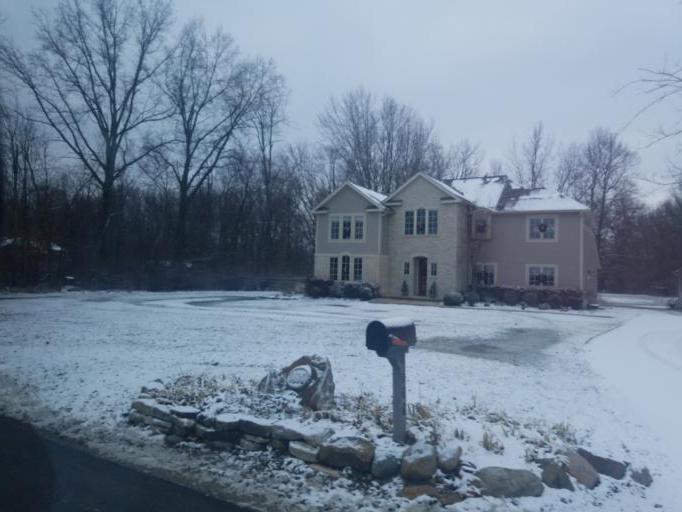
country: US
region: Ohio
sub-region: Franklin County
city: New Albany
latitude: 40.0383
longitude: -82.8170
